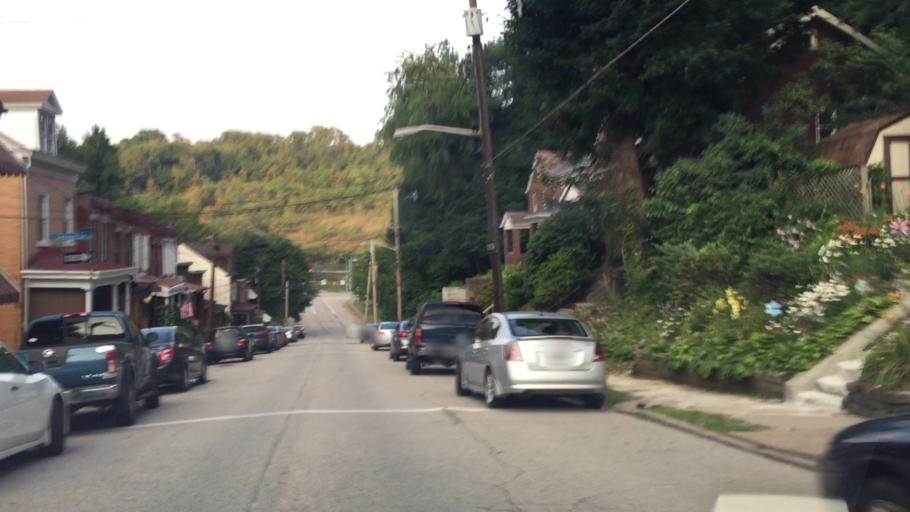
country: US
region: Pennsylvania
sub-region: Allegheny County
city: Millvale
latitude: 40.4852
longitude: -80.0122
